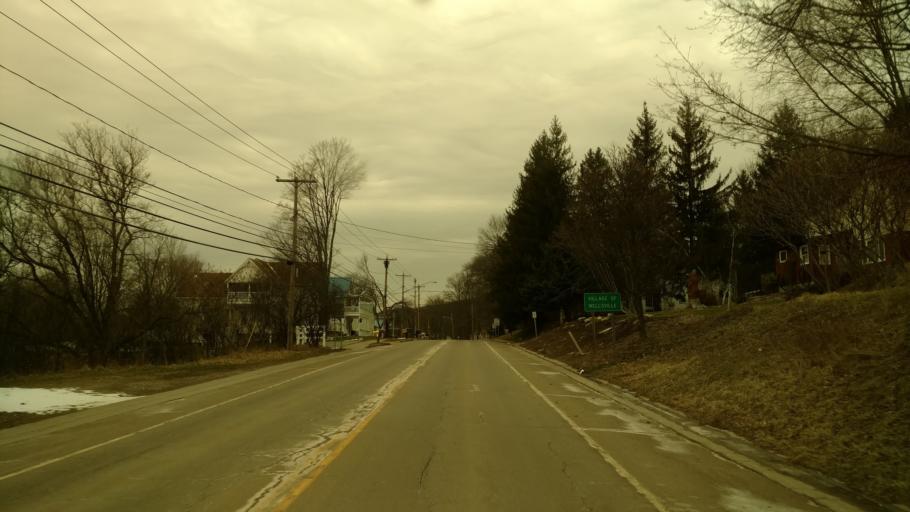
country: US
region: New York
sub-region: Allegany County
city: Wellsville
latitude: 42.1100
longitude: -77.9316
